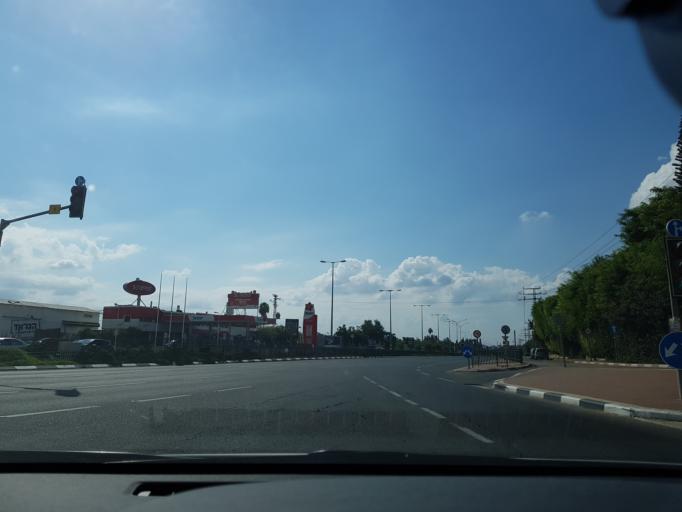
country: IL
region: Central District
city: Ness Ziona
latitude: 31.9479
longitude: 34.8013
